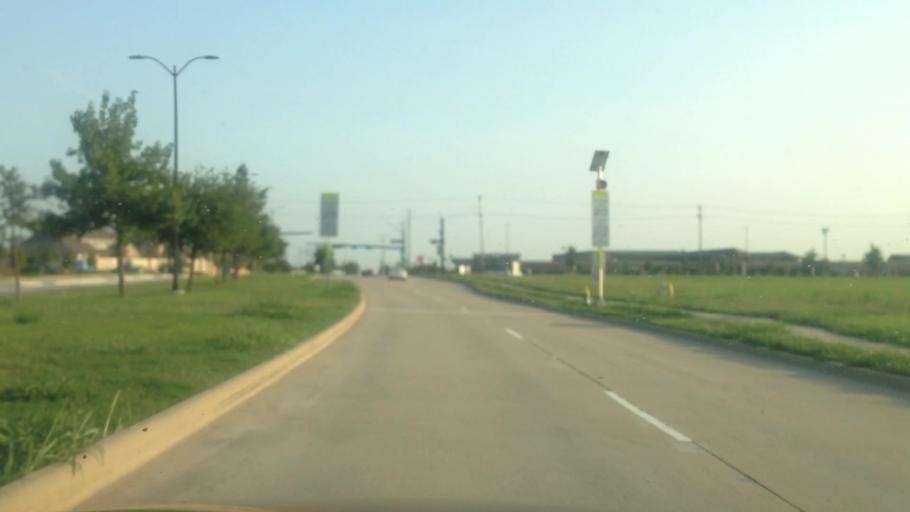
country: US
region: Texas
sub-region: Collin County
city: Frisco
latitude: 33.1346
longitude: -96.8693
